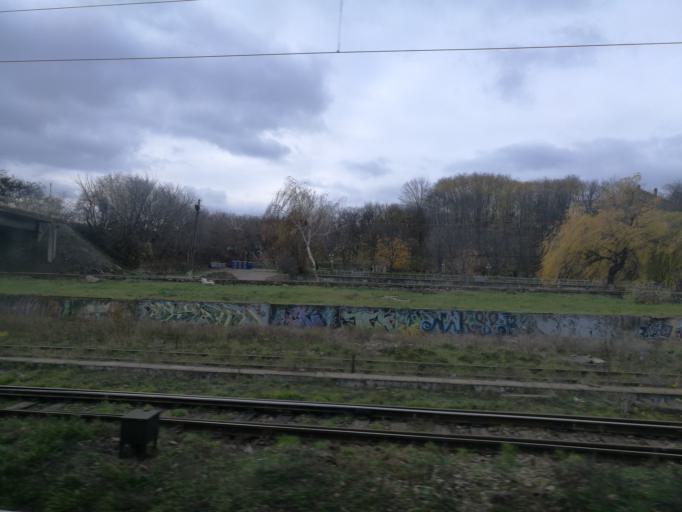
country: RO
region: Iasi
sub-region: Municipiul Pascani
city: Pascani
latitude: 47.2452
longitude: 26.7312
